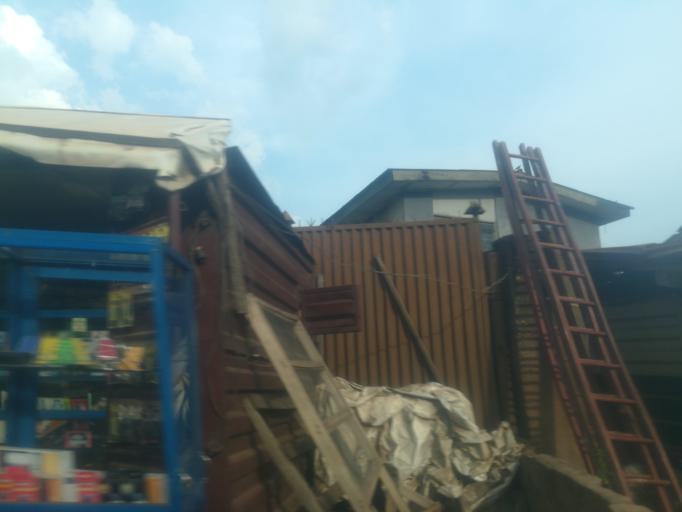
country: NG
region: Ogun
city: Abeokuta
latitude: 7.1488
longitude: 3.3098
